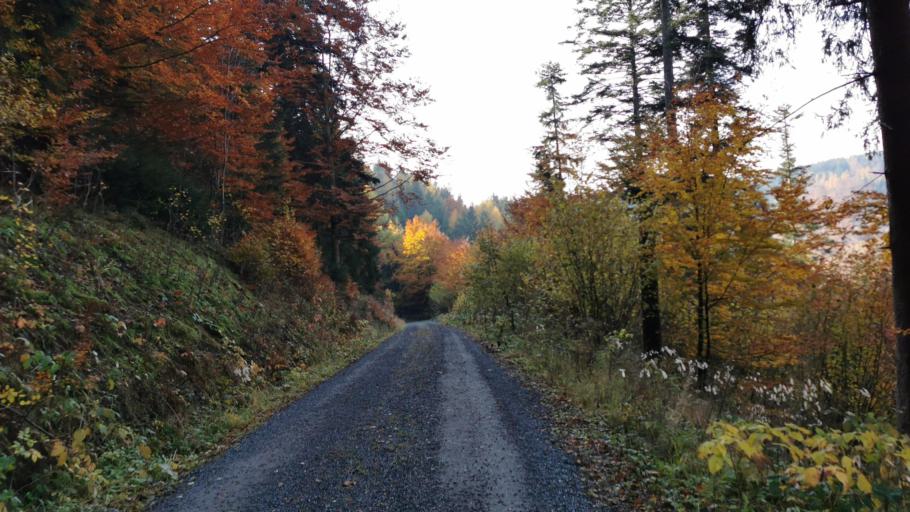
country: DE
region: Bavaria
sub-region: Upper Franconia
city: Nordhalben
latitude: 50.3605
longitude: 11.4947
